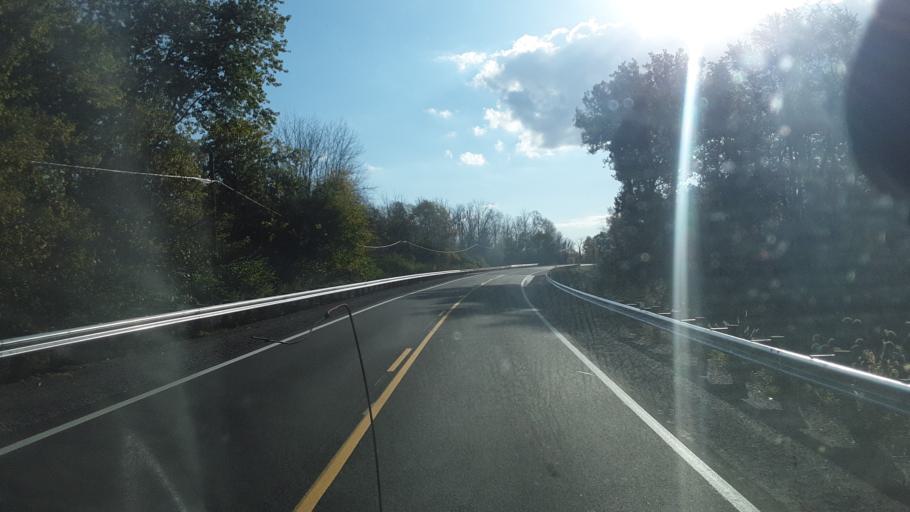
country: US
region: Ohio
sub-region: Fayette County
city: Washington Court House
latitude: 39.5837
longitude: -83.4860
